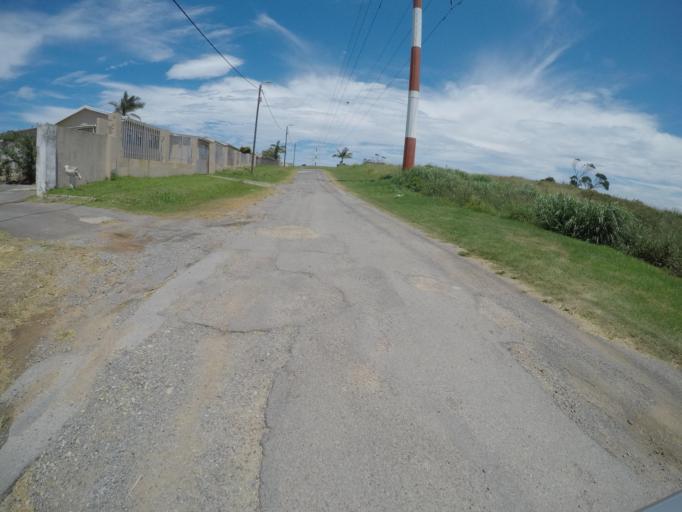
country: ZA
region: Eastern Cape
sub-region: Buffalo City Metropolitan Municipality
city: East London
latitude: -33.0322
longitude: 27.8481
